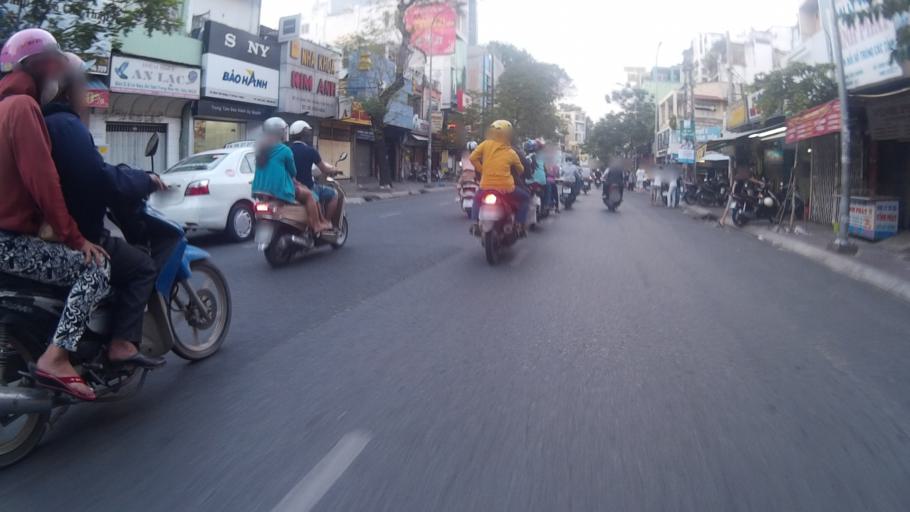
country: VN
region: Ho Chi Minh City
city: Quan Mot
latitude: 10.7911
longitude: 106.6966
